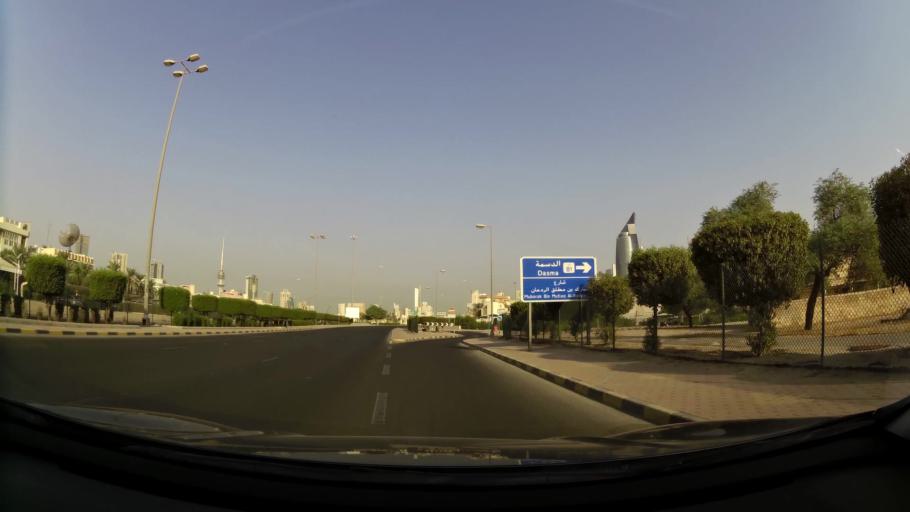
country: KW
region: Al Asimah
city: Ad Dasmah
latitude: 29.3627
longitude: 47.9955
